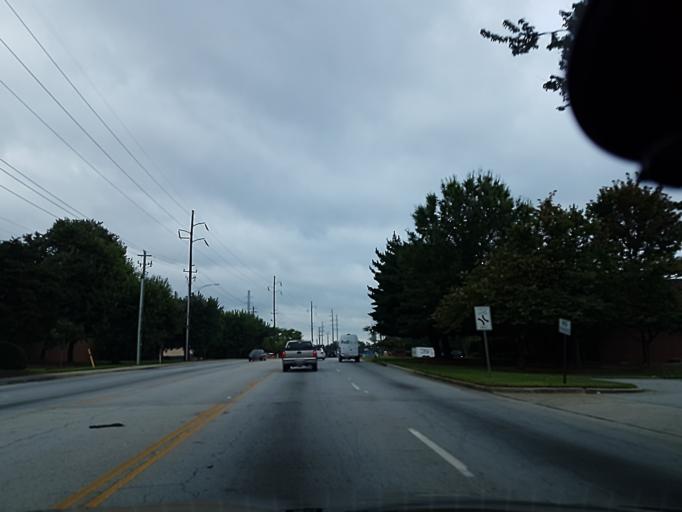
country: US
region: Georgia
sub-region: DeKalb County
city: Stone Mountain
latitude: 33.8284
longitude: -84.1961
